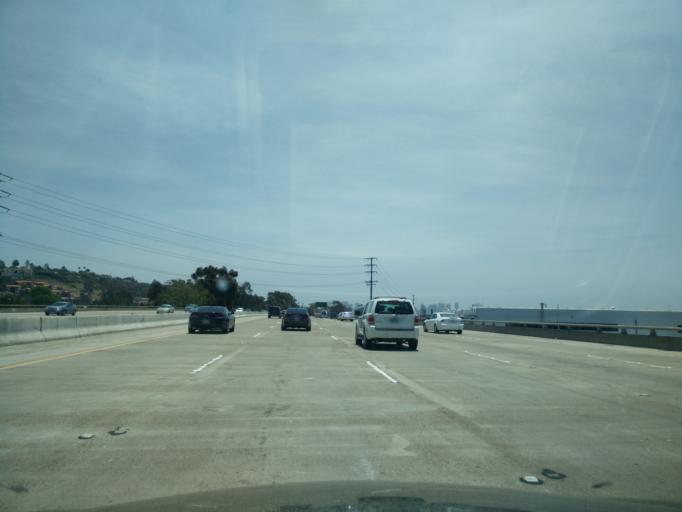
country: US
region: California
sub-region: San Diego County
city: San Diego
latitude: 32.7535
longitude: -117.2000
